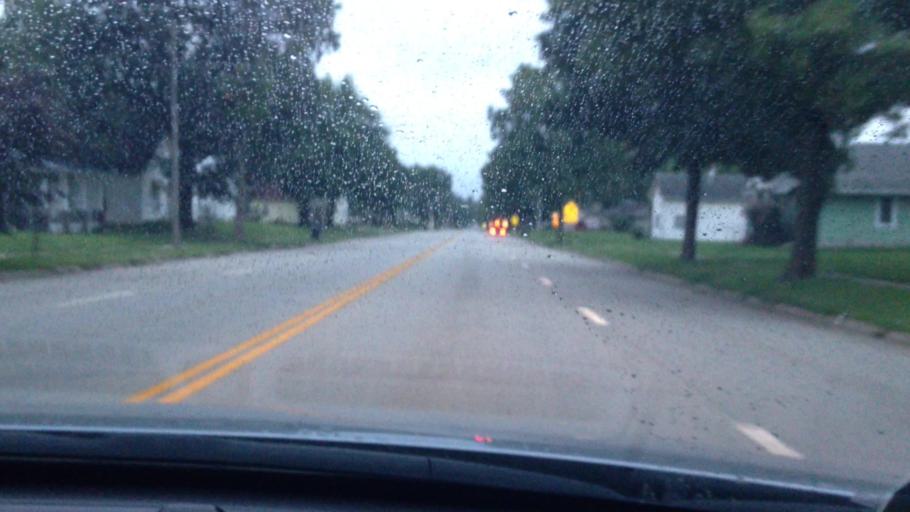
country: US
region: Kansas
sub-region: Brown County
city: Horton
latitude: 39.6706
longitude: -95.5273
